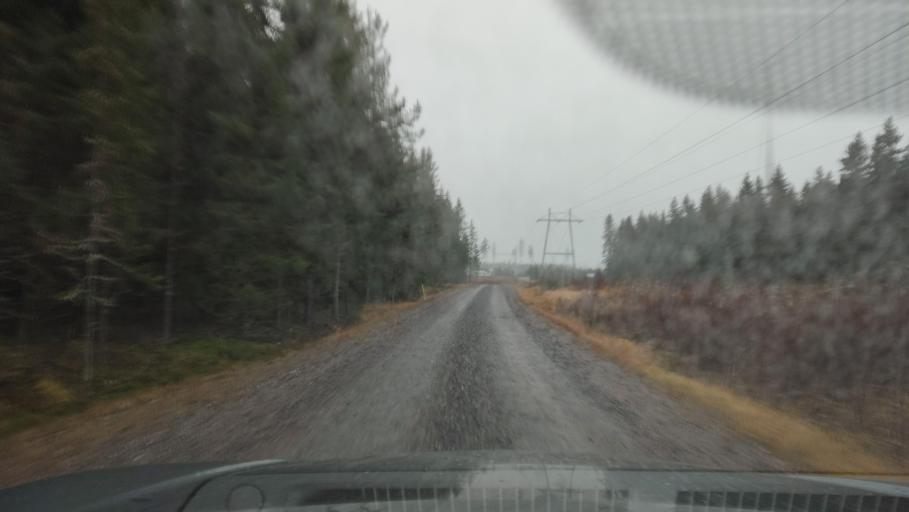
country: FI
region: Southern Ostrobothnia
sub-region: Suupohja
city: Karijoki
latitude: 62.2111
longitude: 21.7299
